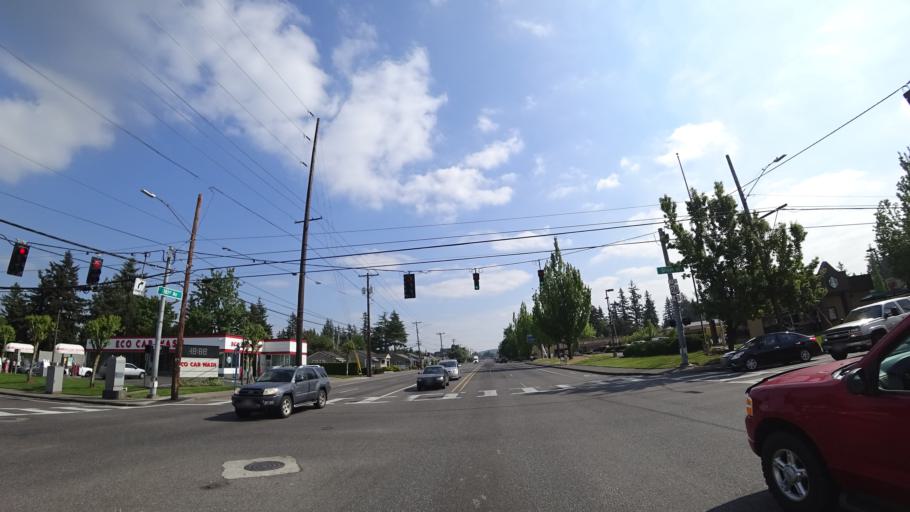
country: US
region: Oregon
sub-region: Multnomah County
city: Fairview
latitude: 45.5265
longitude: -122.4771
